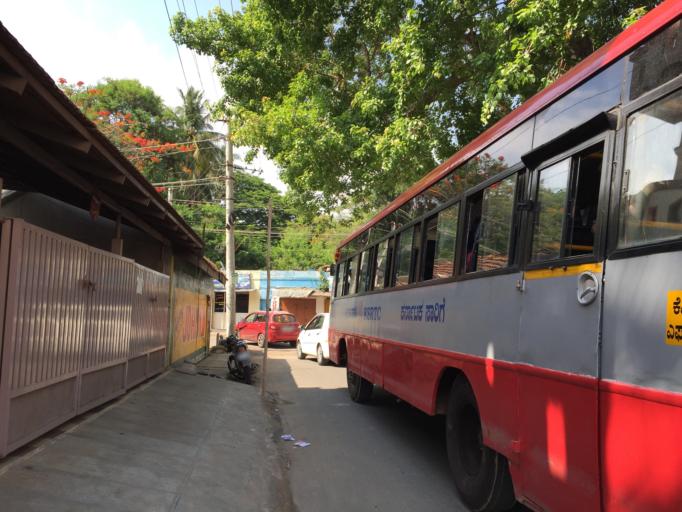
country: IN
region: Karnataka
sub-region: Mysore
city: Mysore
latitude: 12.3054
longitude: 76.6618
